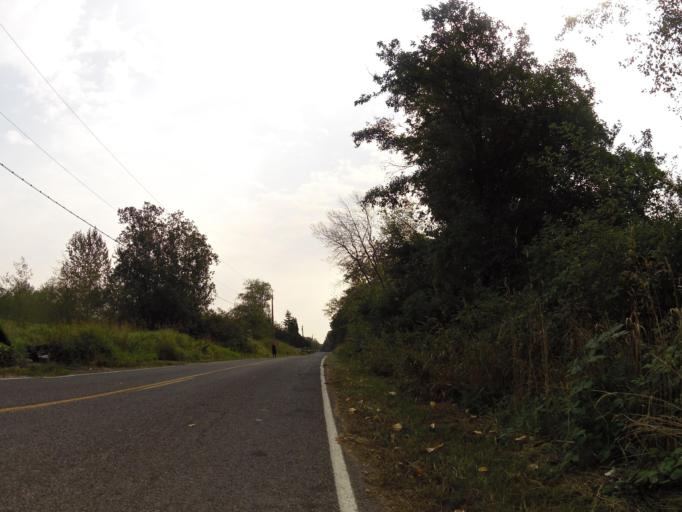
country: US
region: Washington
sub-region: Whatcom County
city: Ferndale
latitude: 48.8075
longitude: -122.6747
